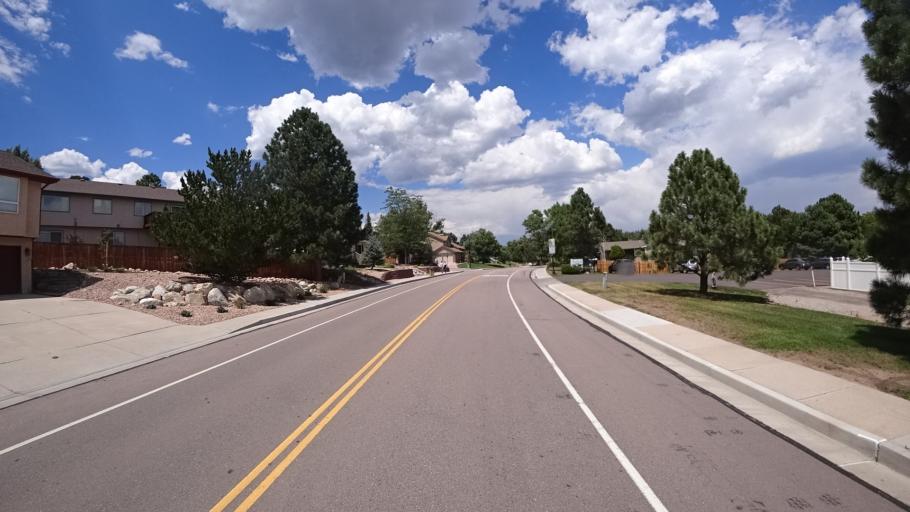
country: US
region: Colorado
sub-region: El Paso County
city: Air Force Academy
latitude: 38.9319
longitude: -104.8335
